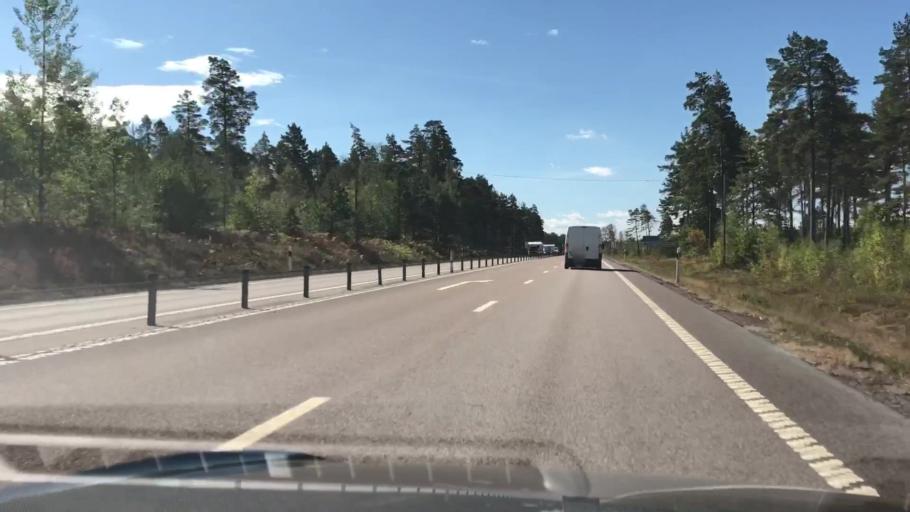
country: SE
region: Kalmar
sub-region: Monsteras Kommun
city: Moensteras
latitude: 57.0863
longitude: 16.4855
